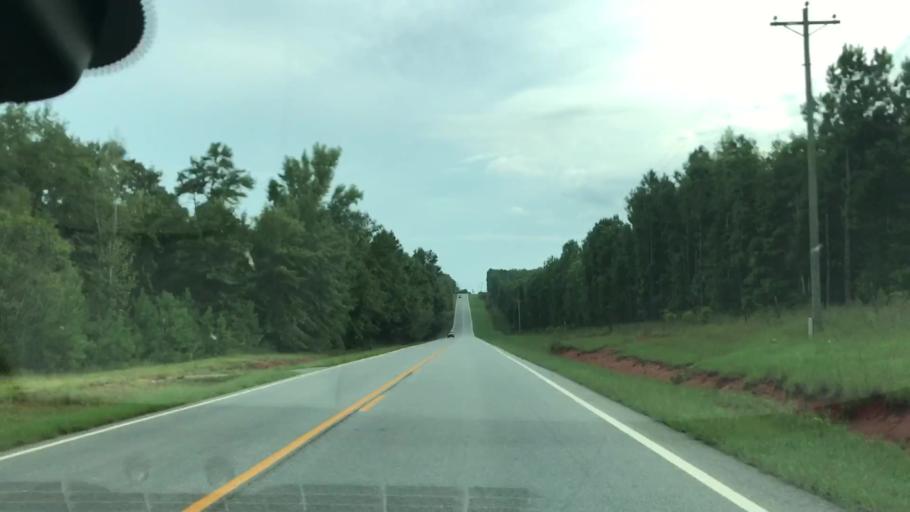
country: US
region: Georgia
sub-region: Quitman County
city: Georgetown
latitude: 31.8361
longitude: -85.0817
